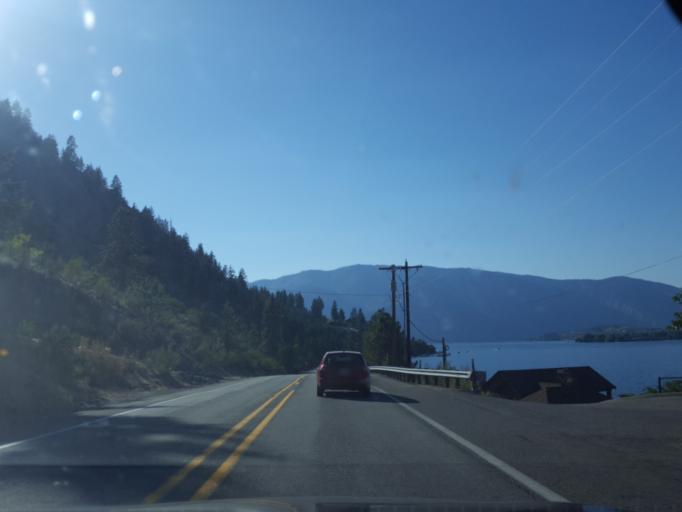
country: US
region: Washington
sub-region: Chelan County
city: Manson
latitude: 47.8538
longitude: -120.1397
